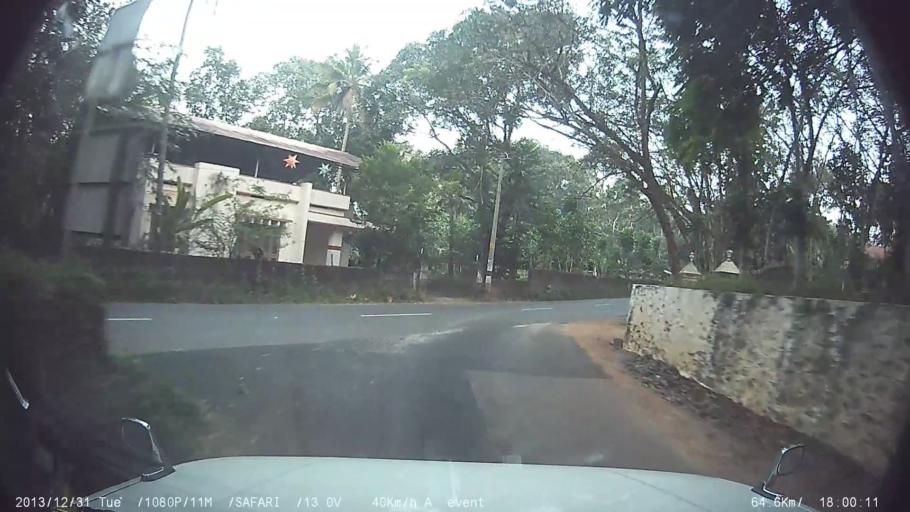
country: IN
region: Kerala
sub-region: Ernakulam
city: Piravam
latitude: 9.7614
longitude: 76.5226
